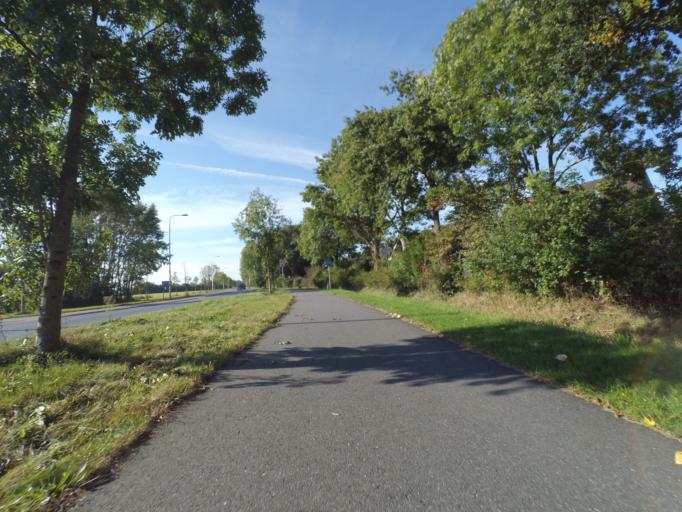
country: NL
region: Gelderland
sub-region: Gemeente Nijkerk
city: Nijkerk
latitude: 52.2119
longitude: 5.5016
